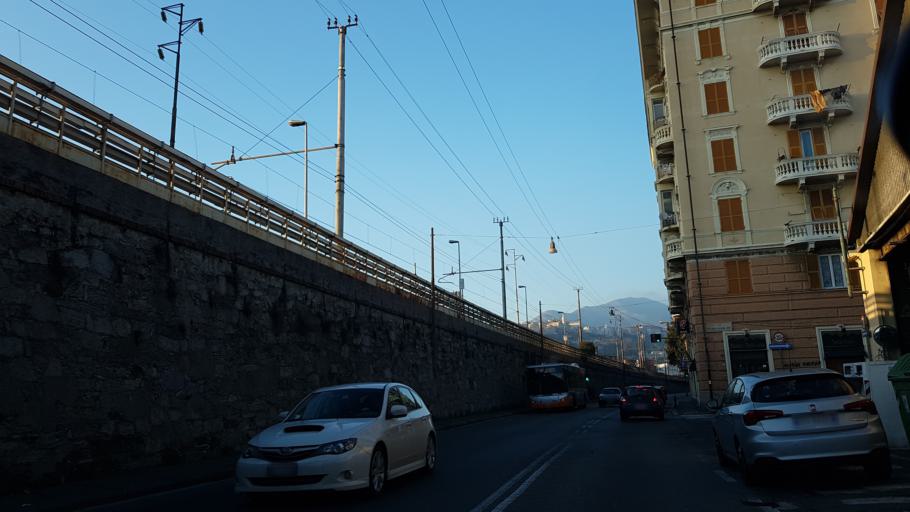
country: IT
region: Liguria
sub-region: Provincia di Genova
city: San Teodoro
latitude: 44.4148
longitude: 8.8862
